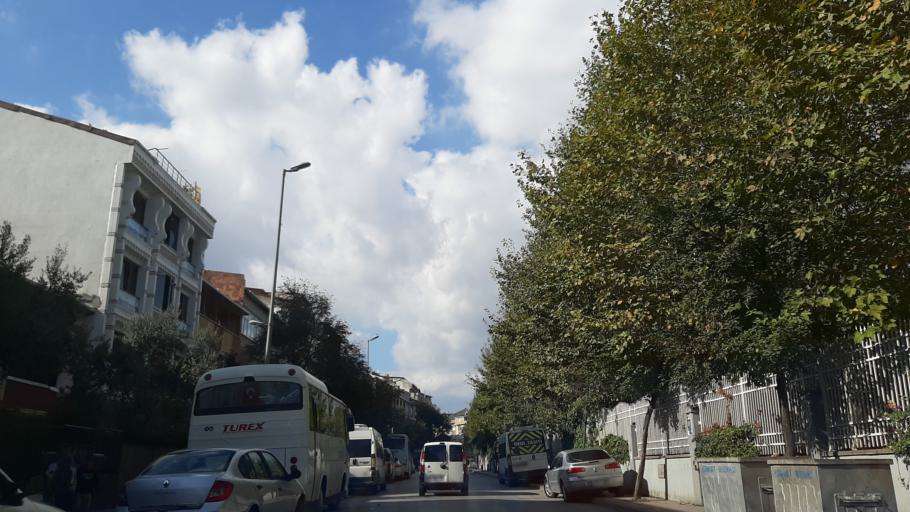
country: TR
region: Istanbul
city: Esenyurt
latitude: 41.0355
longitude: 28.6590
